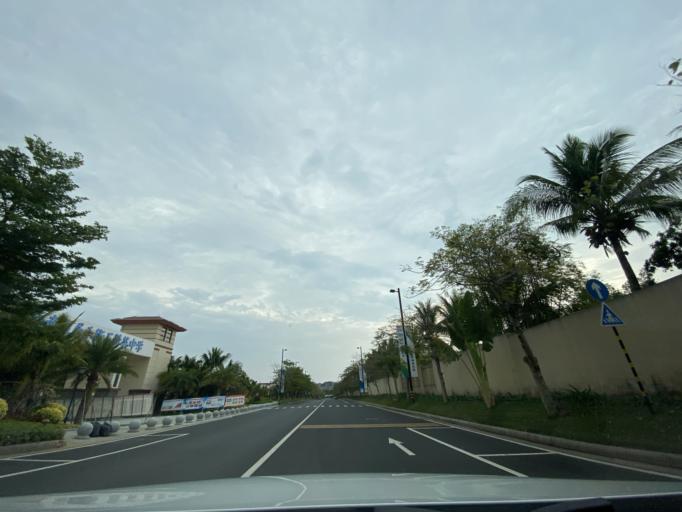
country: CN
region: Hainan
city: Yingzhou
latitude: 18.4046
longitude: 109.8532
